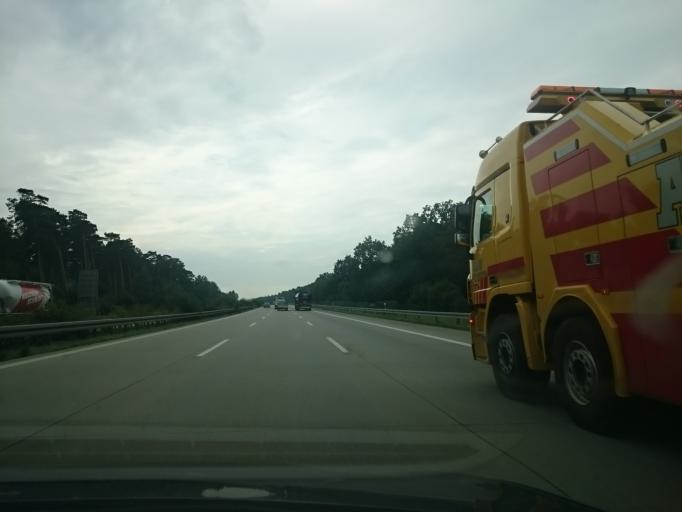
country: DE
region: Brandenburg
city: Niemegk
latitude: 52.0785
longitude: 12.6656
